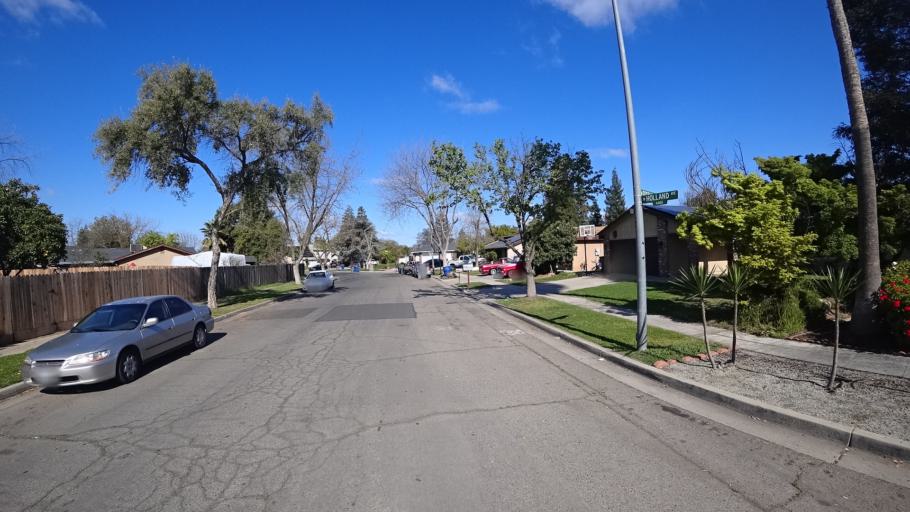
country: US
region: California
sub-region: Fresno County
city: West Park
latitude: 36.7972
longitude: -119.8738
